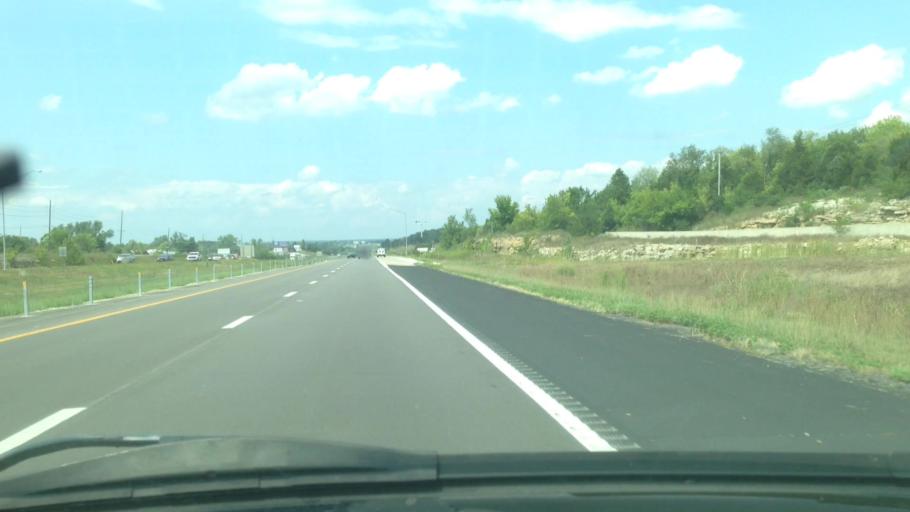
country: US
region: Missouri
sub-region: Lincoln County
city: Moscow Mills
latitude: 38.9099
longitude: -90.9235
